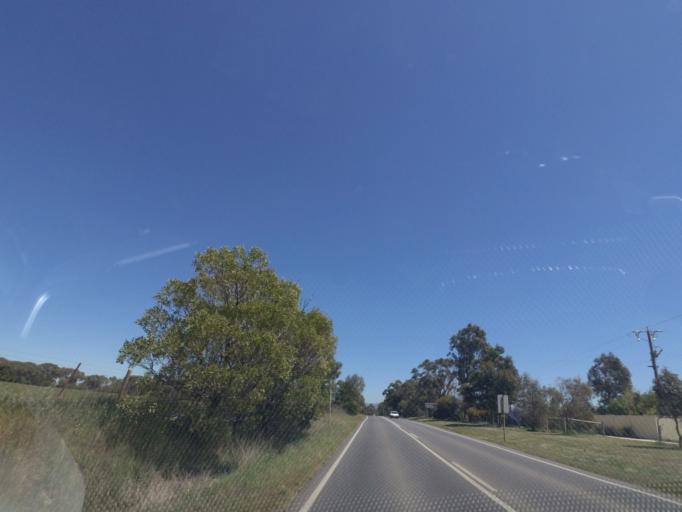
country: AU
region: Victoria
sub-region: Whittlesea
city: Whittlesea
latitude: -37.2944
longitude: 144.9363
